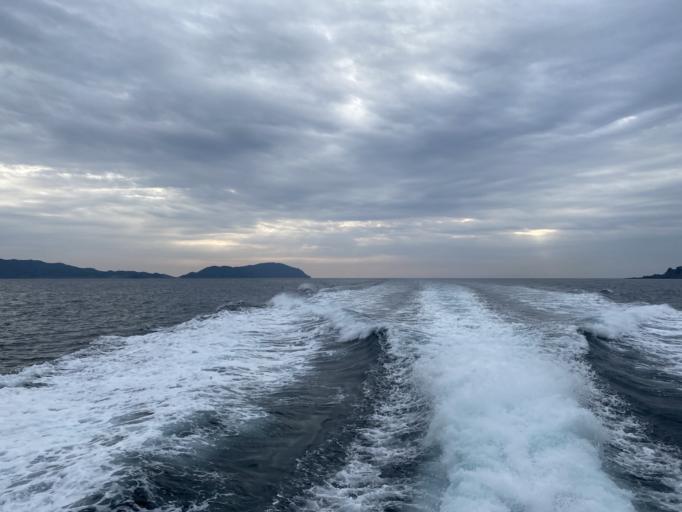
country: JP
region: Nagasaki
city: Nagasaki-shi
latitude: 32.6412
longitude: 129.7627
